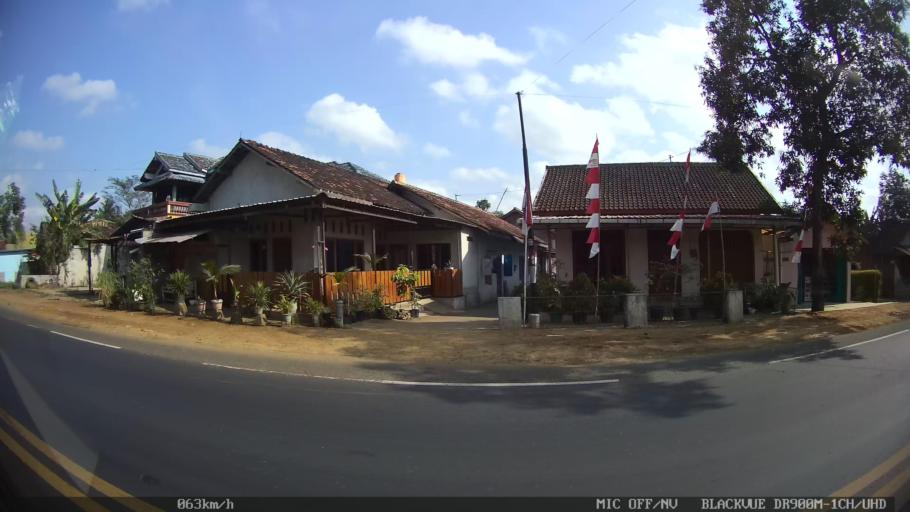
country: ID
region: Daerah Istimewa Yogyakarta
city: Godean
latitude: -7.8255
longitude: 110.2278
